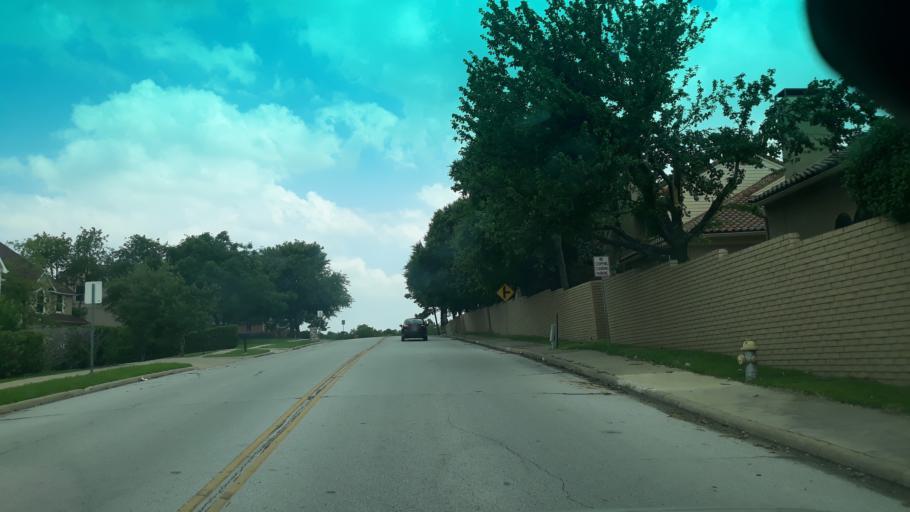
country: US
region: Texas
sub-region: Dallas County
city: Irving
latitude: 32.8619
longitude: -96.9802
